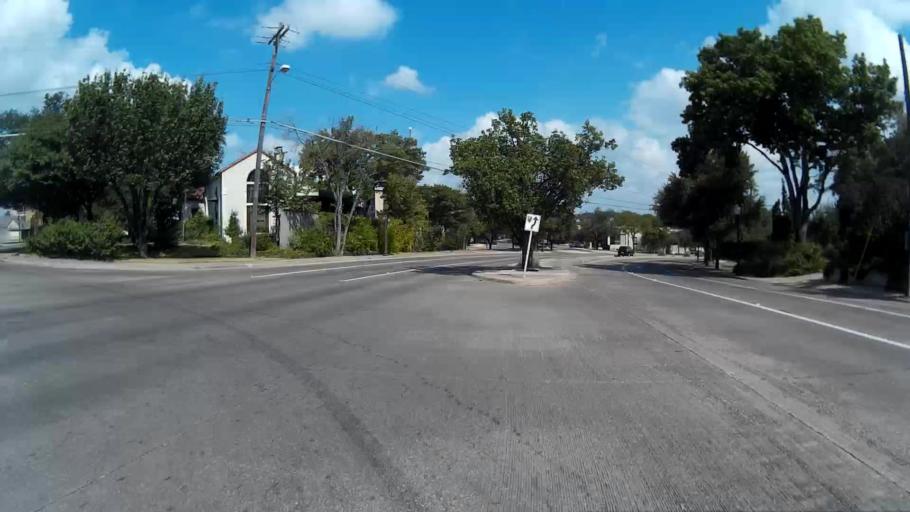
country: US
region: Texas
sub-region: Dallas County
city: Highland Park
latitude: 32.8109
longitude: -96.7530
